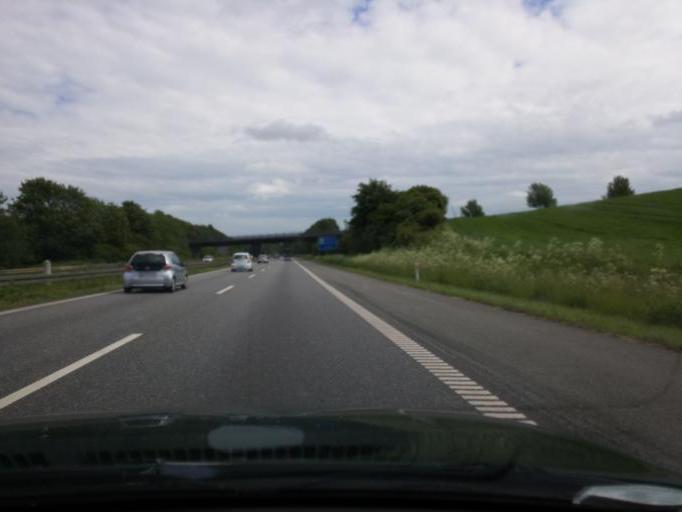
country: DK
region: South Denmark
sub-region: Assens Kommune
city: Arup
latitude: 55.4149
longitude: 10.0363
